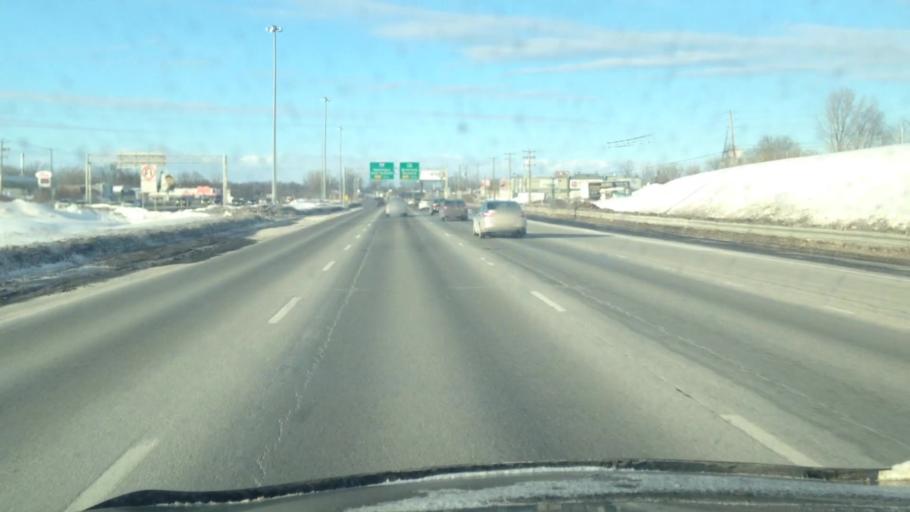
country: CA
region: Quebec
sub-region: Laurentides
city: Boisbriand
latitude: 45.6005
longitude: -73.8045
